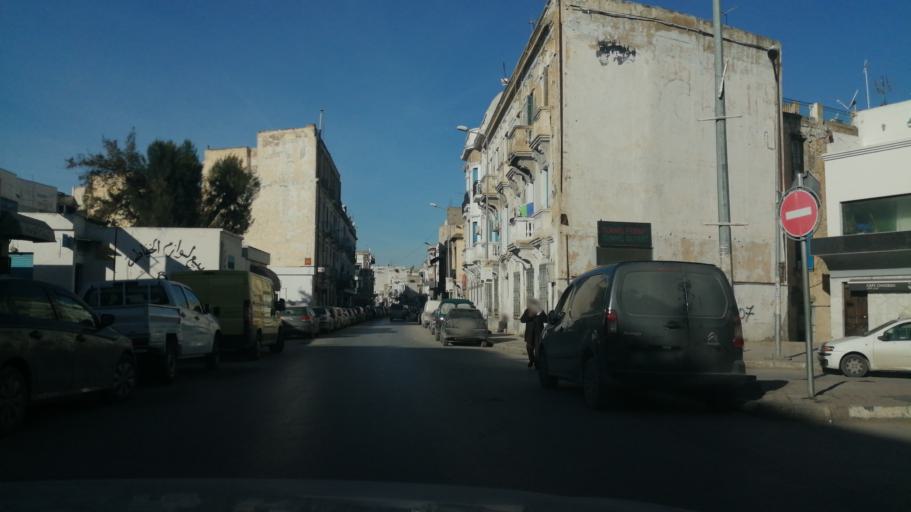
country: TN
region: Tunis
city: Tunis
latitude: 36.8056
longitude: 10.1738
